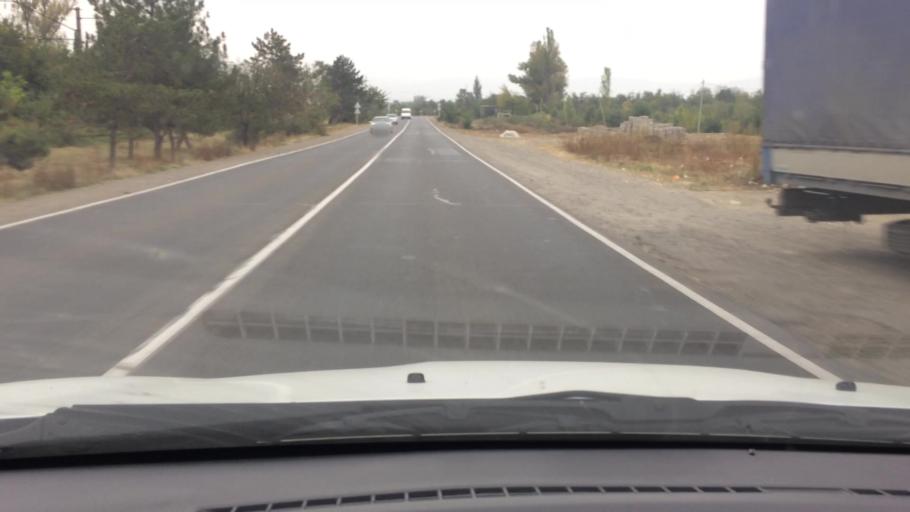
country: GE
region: Kvemo Kartli
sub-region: Marneuli
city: Marneuli
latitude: 41.4123
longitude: 44.8296
